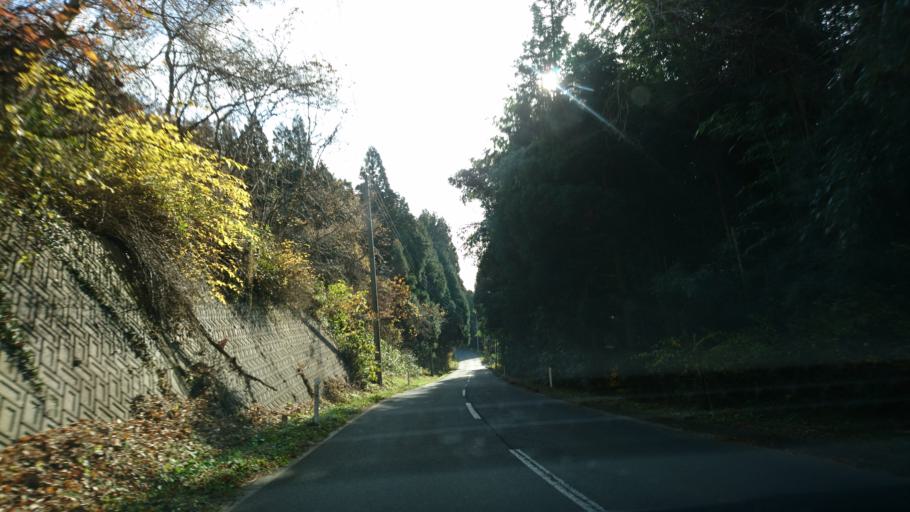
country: JP
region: Iwate
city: Ichinoseki
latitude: 38.8717
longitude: 141.3057
